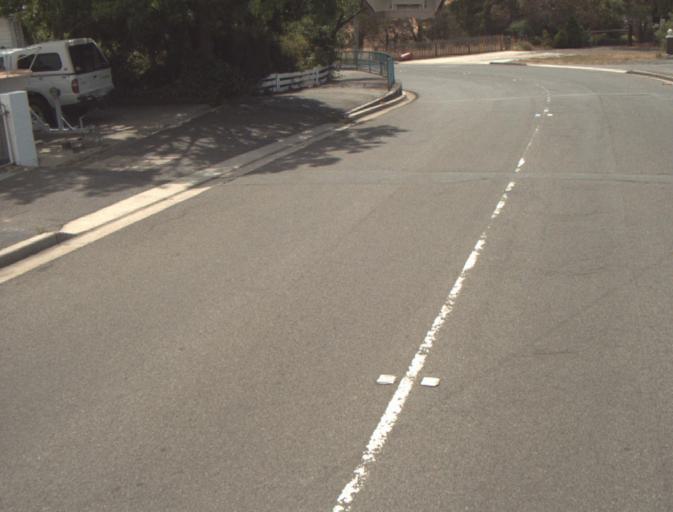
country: AU
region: Tasmania
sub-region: Launceston
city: Newstead
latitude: -41.4521
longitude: 147.2025
